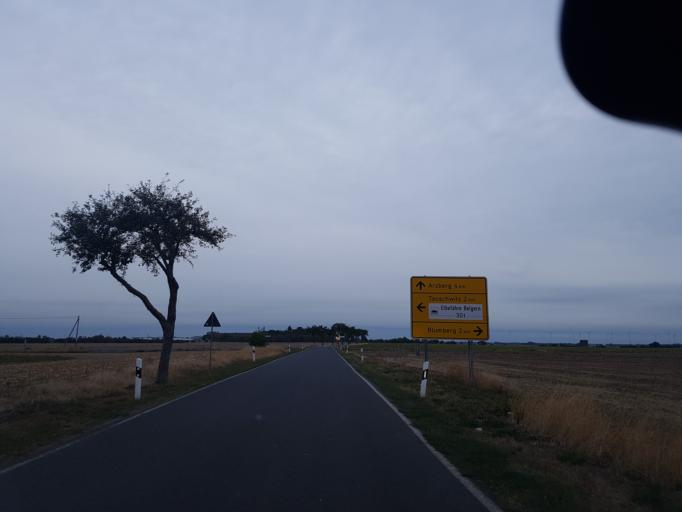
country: DE
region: Saxony
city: Arzberg
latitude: 51.5040
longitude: 13.1648
